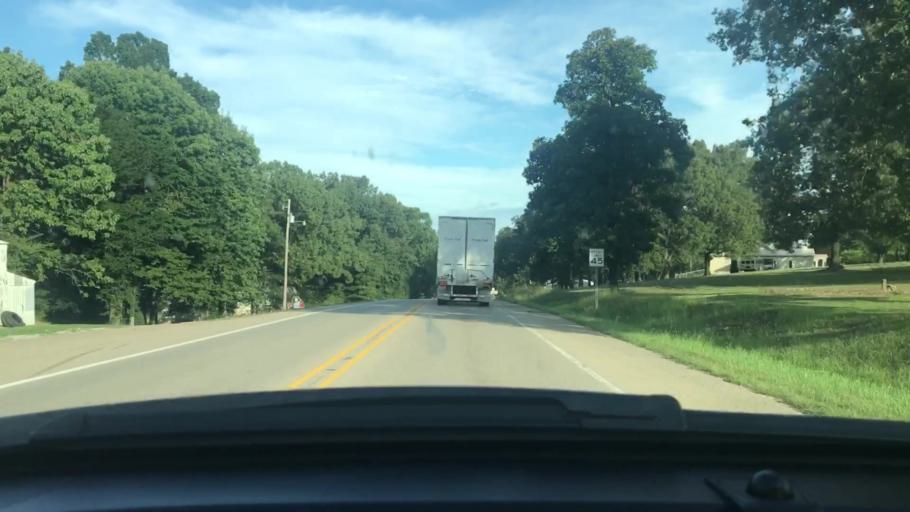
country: US
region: Arkansas
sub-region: Sharp County
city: Cherokee Village
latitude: 36.2387
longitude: -91.2591
